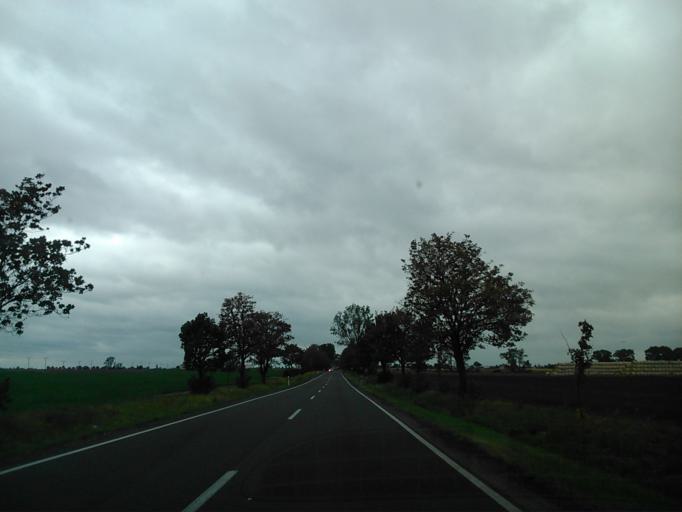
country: PL
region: Kujawsko-Pomorskie
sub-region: Powiat inowroclawski
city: Kruszwica
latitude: 52.6855
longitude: 18.2975
